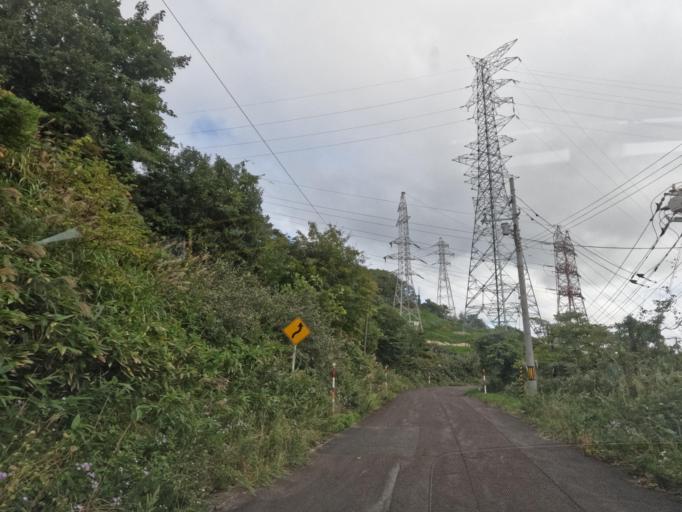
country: JP
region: Hokkaido
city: Muroran
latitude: 42.3279
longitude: 141.0014
